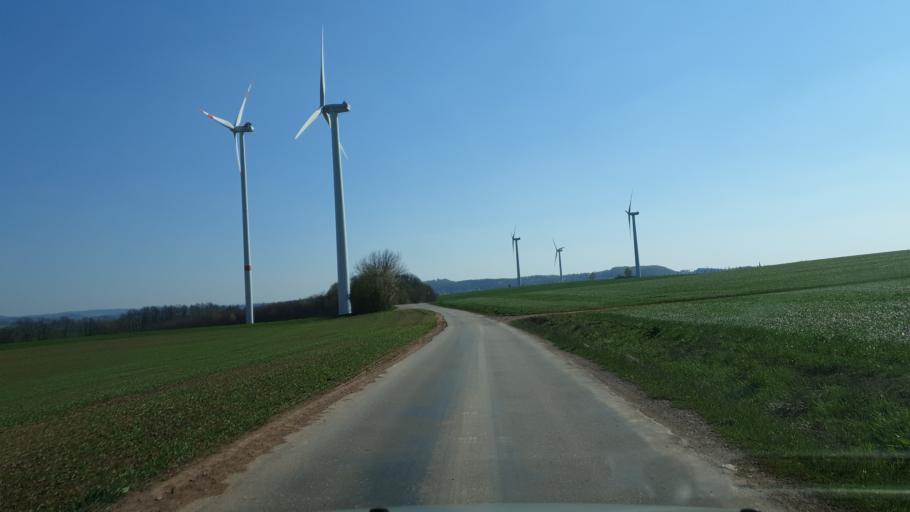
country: DE
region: Saxony
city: Hohndorf
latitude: 50.7637
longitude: 12.6850
